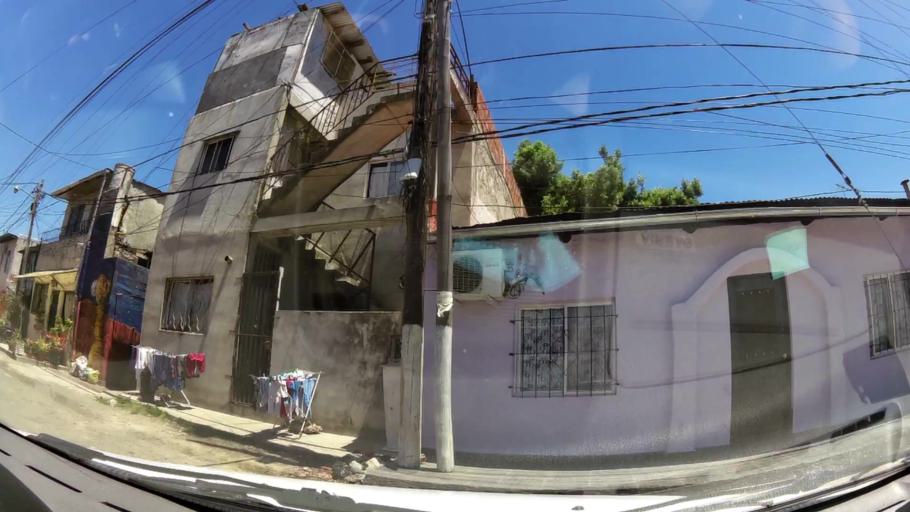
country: AR
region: Buenos Aires
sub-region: Partido de Vicente Lopez
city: Olivos
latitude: -34.4947
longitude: -58.4808
